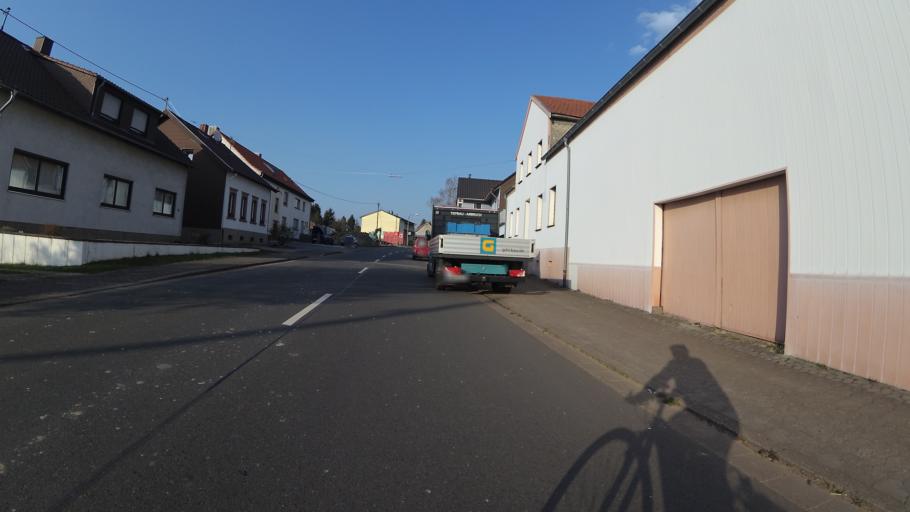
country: DE
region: Saarland
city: Merchweiler
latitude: 49.3453
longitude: 7.0008
